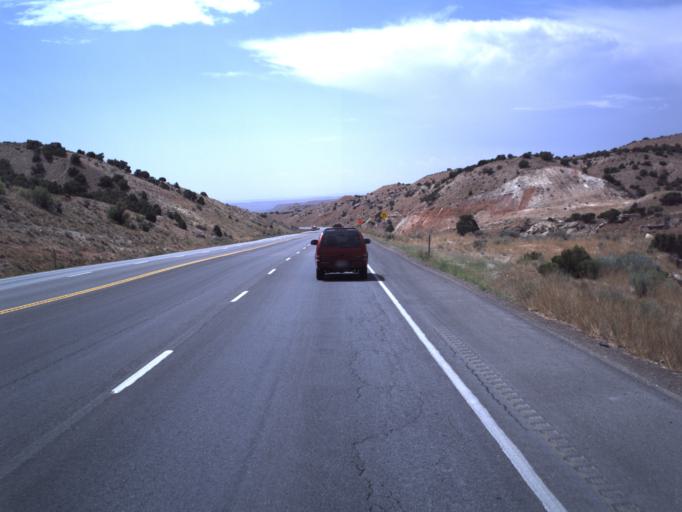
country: US
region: Utah
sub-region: Uintah County
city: Maeser
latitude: 40.4111
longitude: -109.5862
